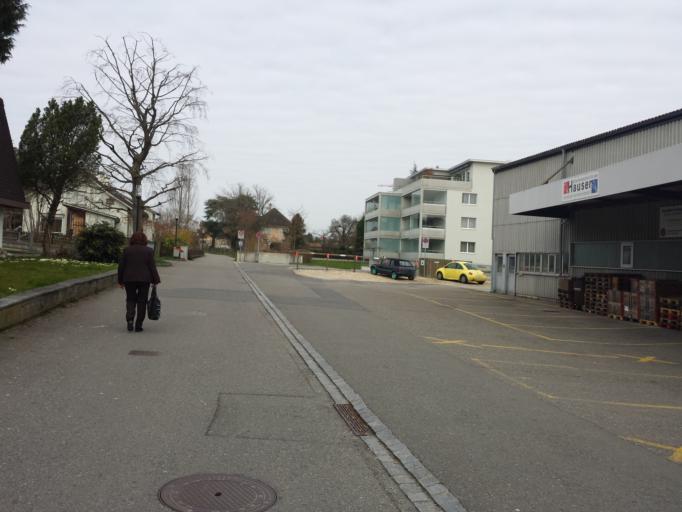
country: CH
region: Thurgau
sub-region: Arbon District
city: Romanshorn
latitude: 47.5667
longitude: 9.3760
